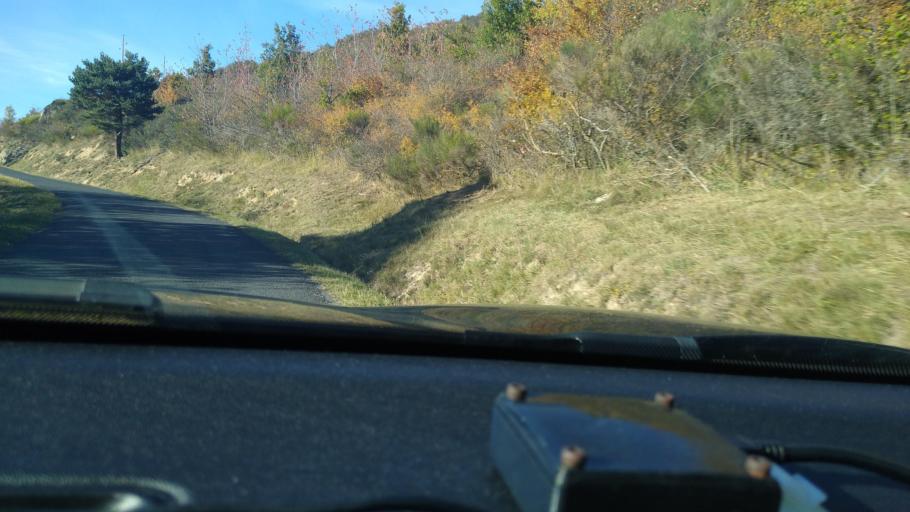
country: FR
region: Languedoc-Roussillon
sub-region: Departement de l'Aude
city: Quillan
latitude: 42.7254
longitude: 2.1211
